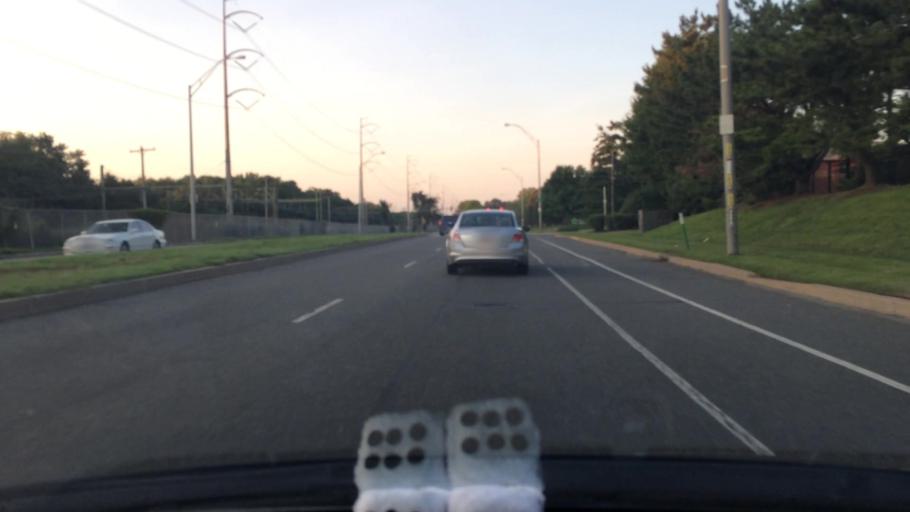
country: US
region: Pennsylvania
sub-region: Delaware County
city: Colwyn
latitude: 39.8857
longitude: -75.2497
